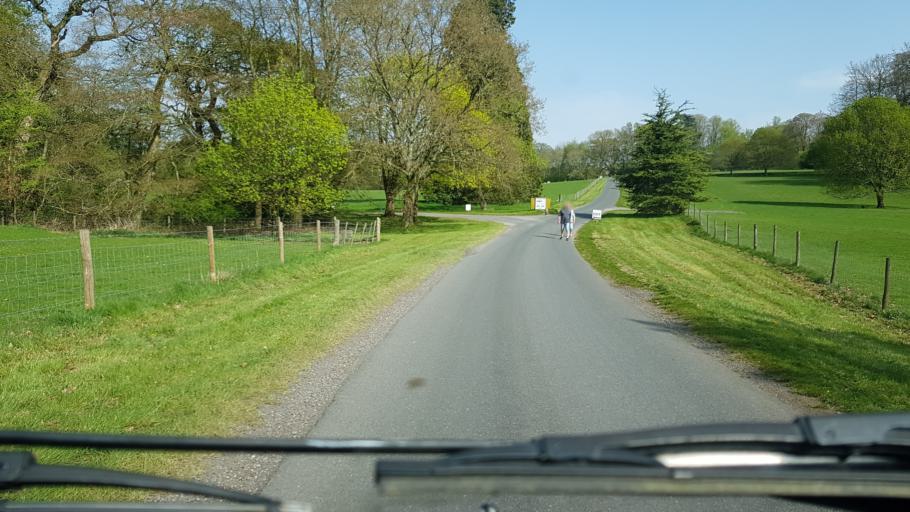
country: GB
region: England
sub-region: Hampshire
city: Highclere
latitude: 51.3311
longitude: -1.3551
